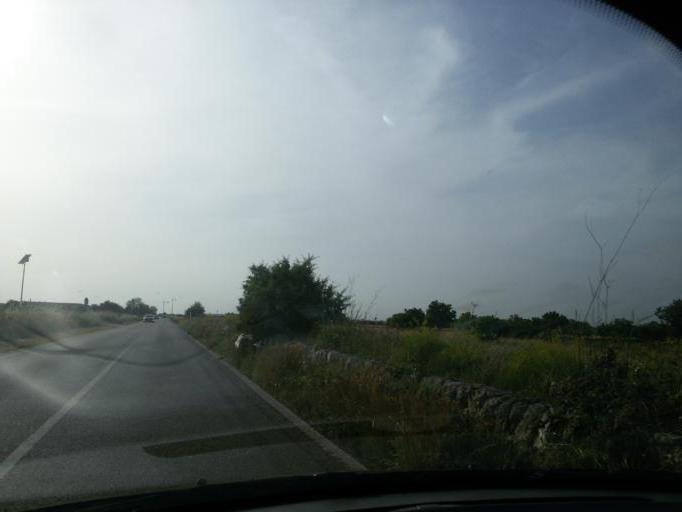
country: IT
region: Apulia
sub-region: Provincia di Lecce
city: Porto Cesareo
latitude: 40.2839
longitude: 17.8834
